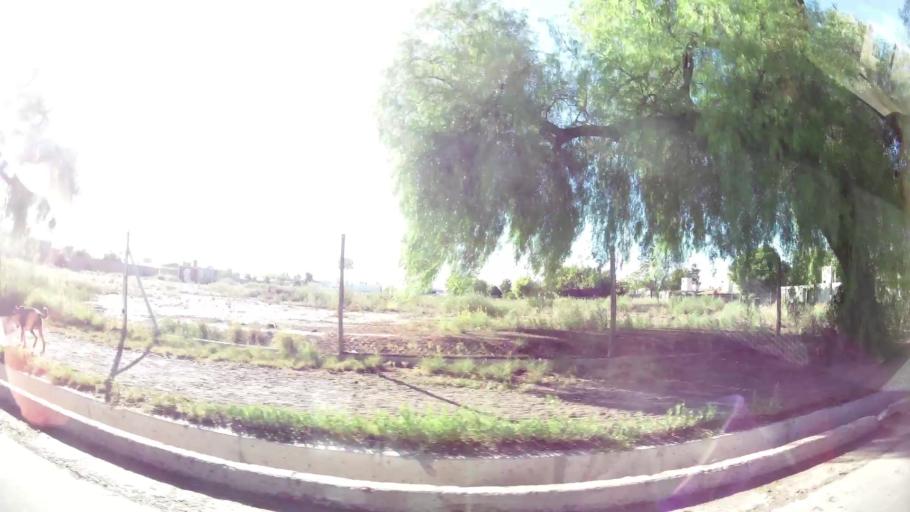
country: AR
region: Mendoza
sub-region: Departamento de Godoy Cruz
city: Godoy Cruz
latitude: -32.9359
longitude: -68.8325
